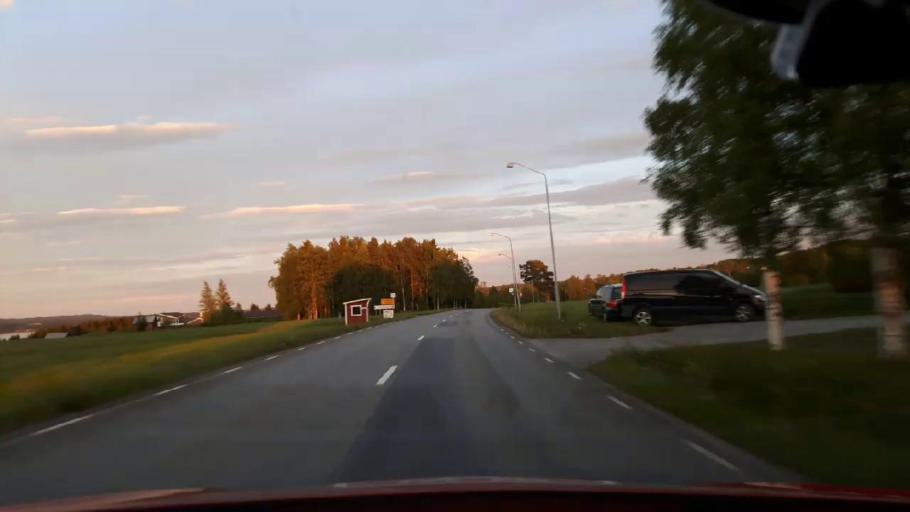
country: SE
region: Jaemtland
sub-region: OEstersunds Kommun
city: Brunflo
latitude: 63.0971
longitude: 14.7449
